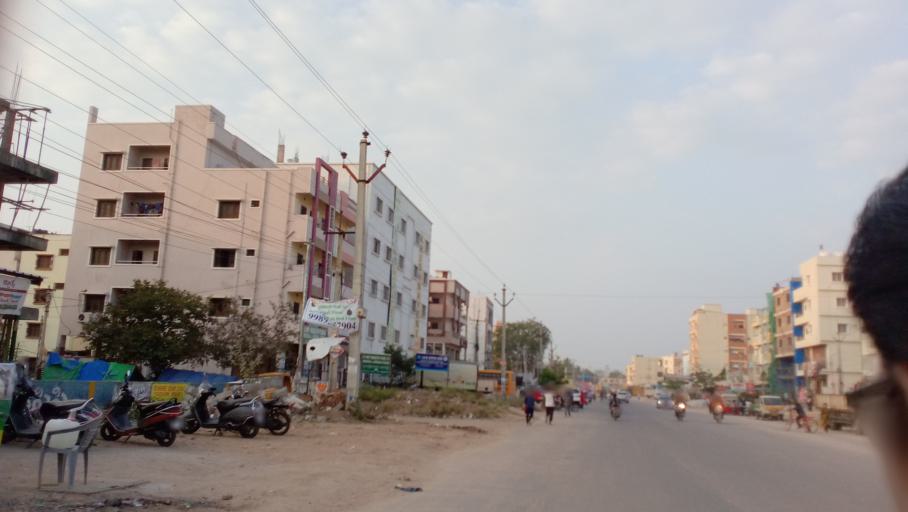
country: IN
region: Telangana
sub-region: Medak
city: Serilingampalle
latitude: 17.5062
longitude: 78.3183
